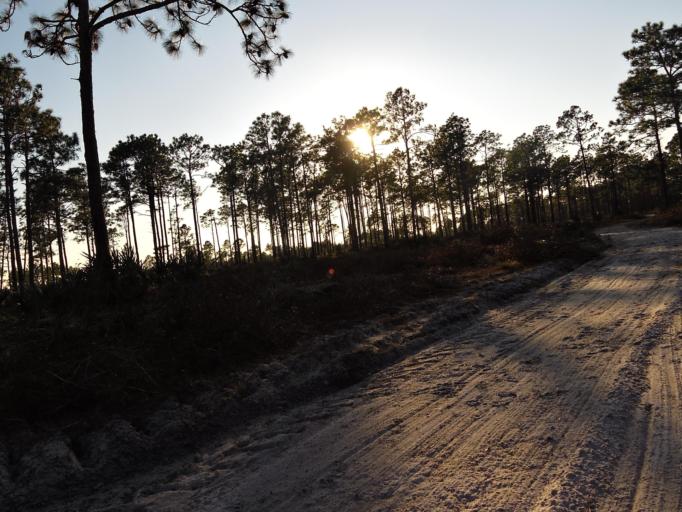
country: US
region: Florida
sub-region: Duval County
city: Atlantic Beach
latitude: 30.4776
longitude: -81.5044
